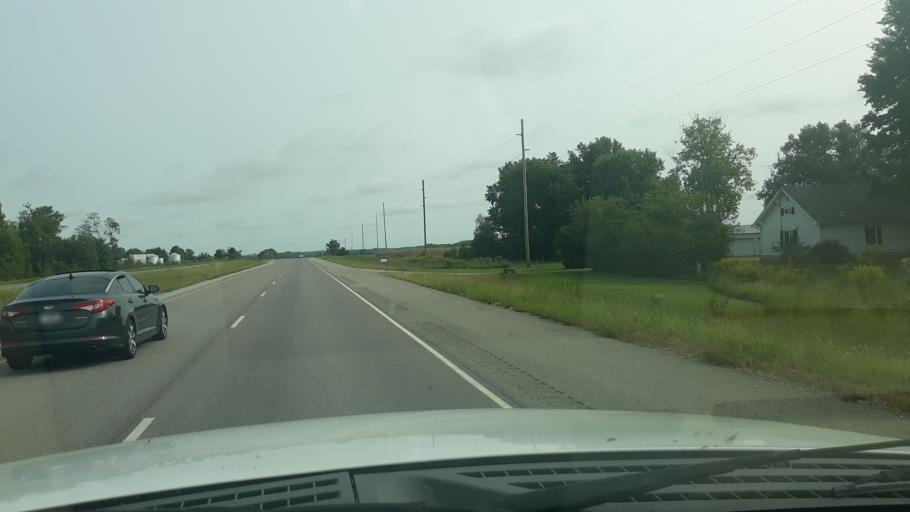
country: US
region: Illinois
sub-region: Saline County
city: Eldorado
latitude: 37.8534
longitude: -88.4079
